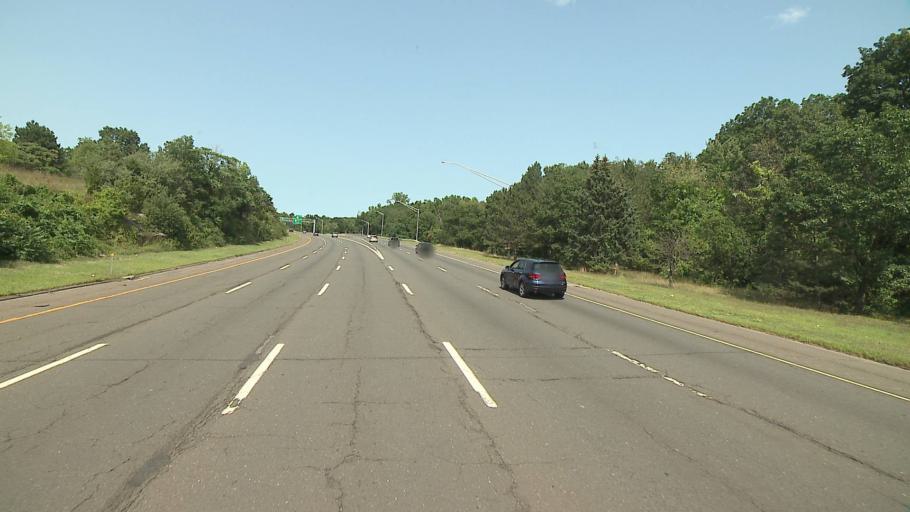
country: US
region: Connecticut
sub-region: Fairfield County
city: Trumbull
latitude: 41.2174
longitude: -73.1813
